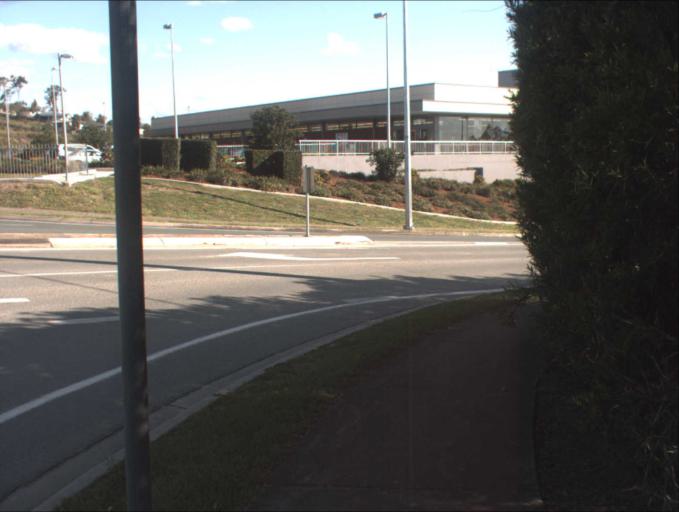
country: AU
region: Queensland
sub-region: Logan
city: Waterford West
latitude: -27.7015
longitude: 153.1585
